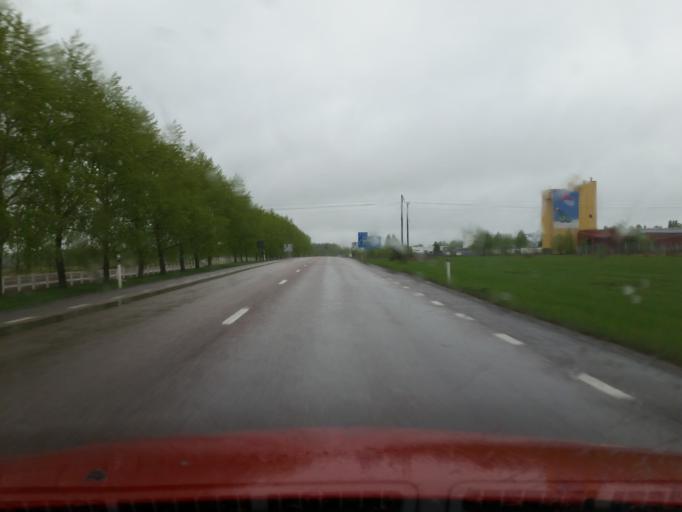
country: SE
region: Dalarna
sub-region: Borlange Kommun
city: Borlaenge
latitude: 60.4458
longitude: 15.4976
